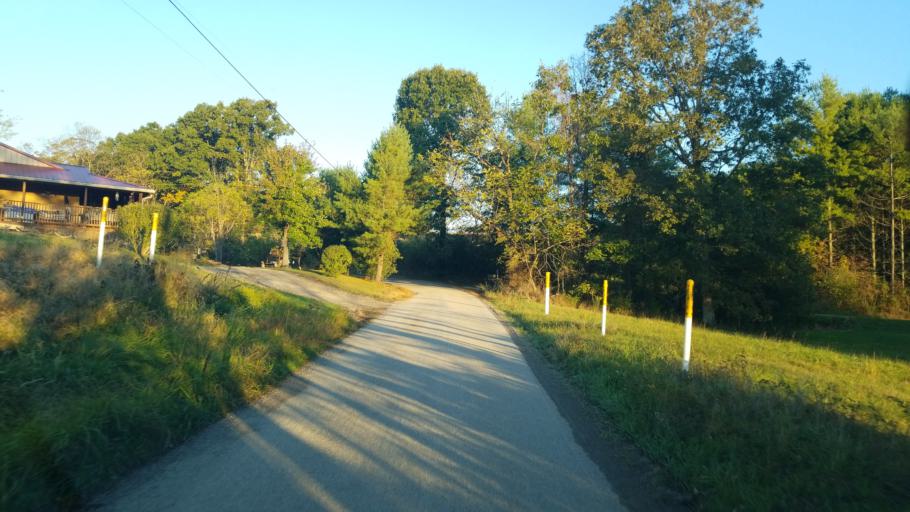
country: US
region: Ohio
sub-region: Jackson County
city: Wellston
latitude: 39.1663
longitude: -82.5423
